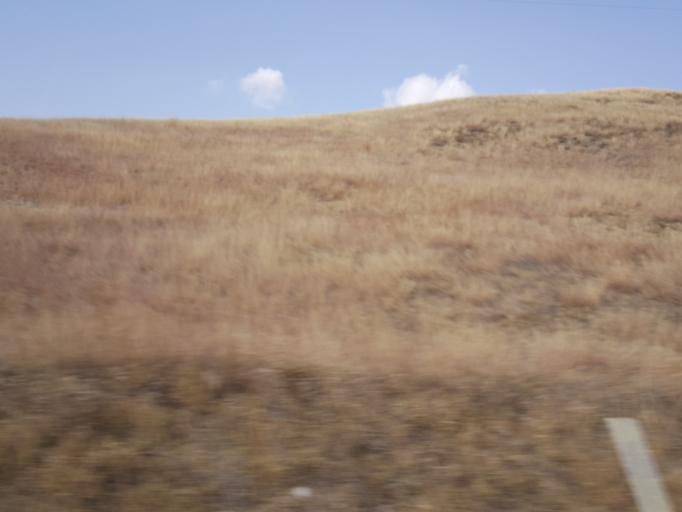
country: TR
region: Corum
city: Bogazkale
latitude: 40.1458
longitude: 34.5786
